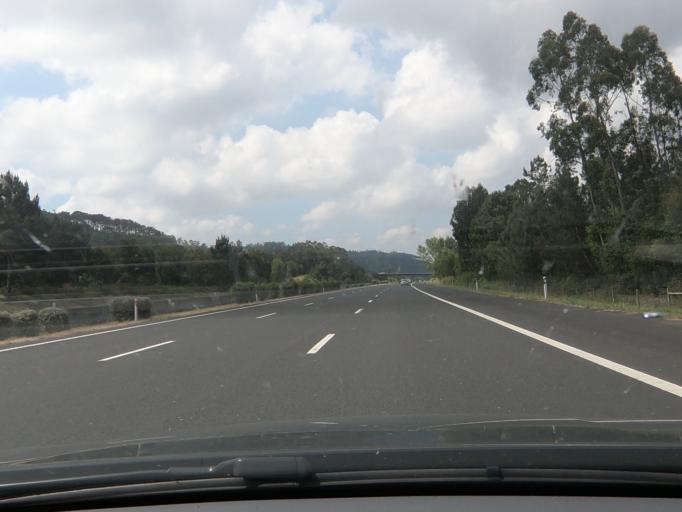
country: PT
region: Leiria
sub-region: Caldas da Rainha
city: Caldas da Rainha
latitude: 39.4756
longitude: -9.1041
